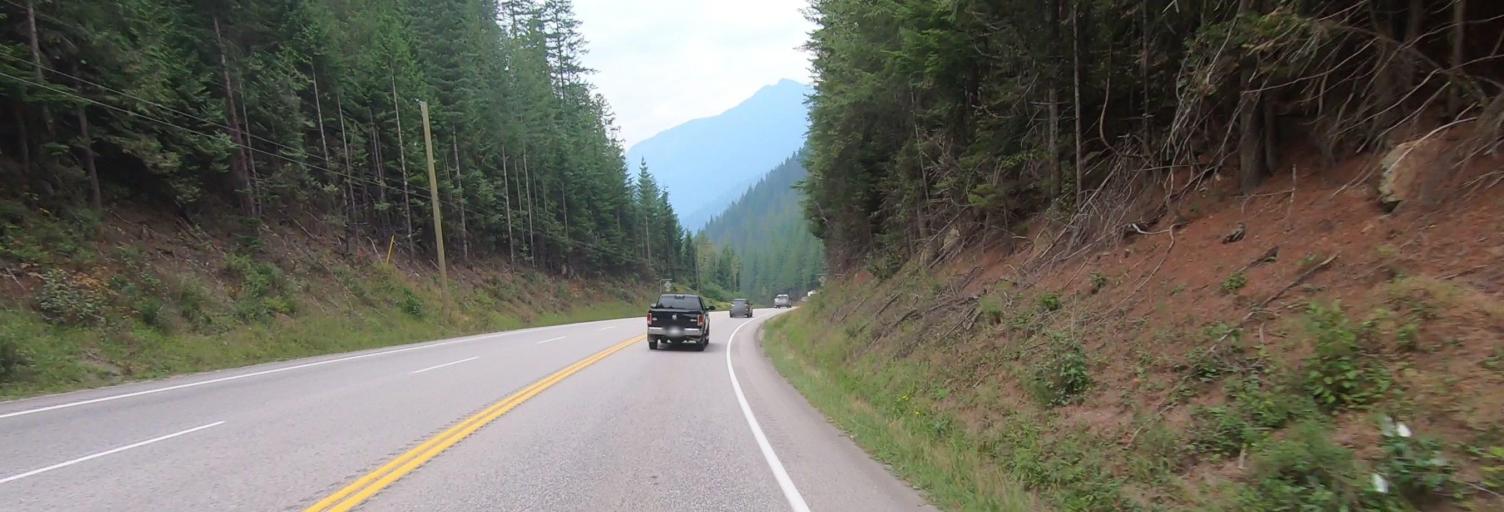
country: CA
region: British Columbia
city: Revelstoke
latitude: 50.9535
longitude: -118.4905
